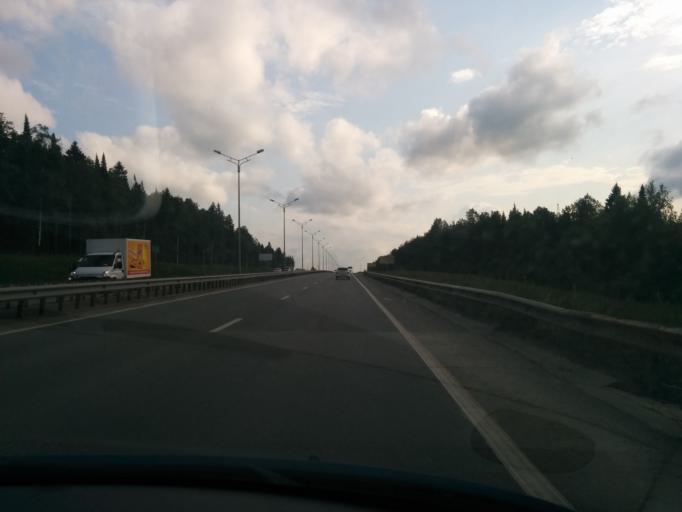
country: RU
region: Perm
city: Ferma
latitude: 58.0085
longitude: 56.3974
